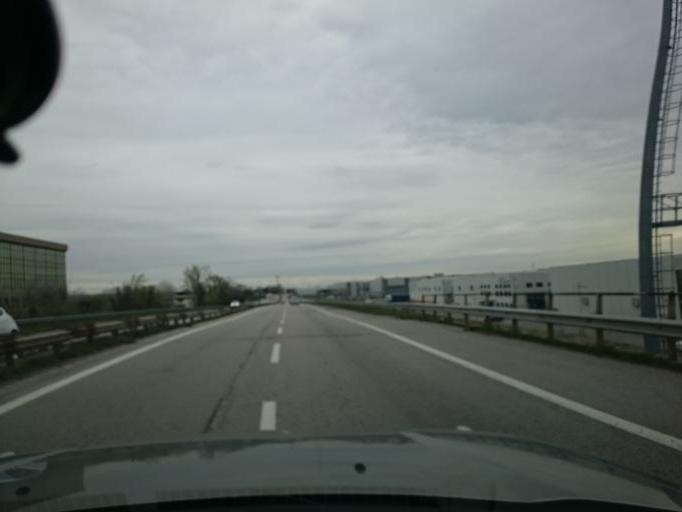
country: IT
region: Veneto
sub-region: Provincia di Padova
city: Ponte San Nicolo
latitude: 45.3958
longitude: 11.9285
